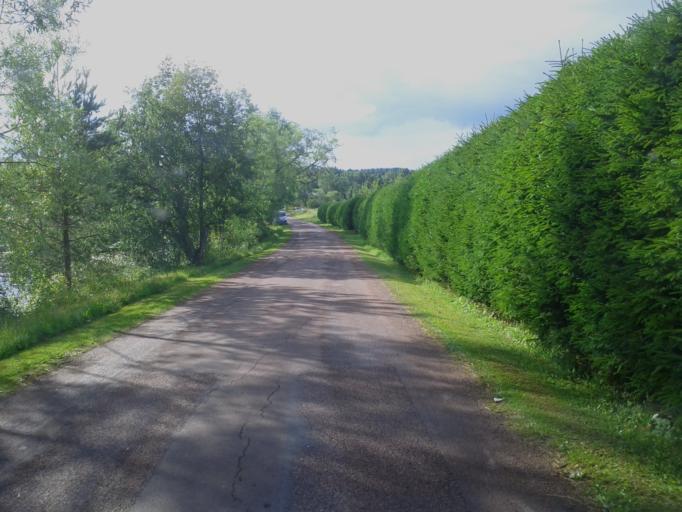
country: SE
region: Dalarna
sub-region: Borlange Kommun
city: Ornas
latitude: 60.5083
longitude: 15.5502
